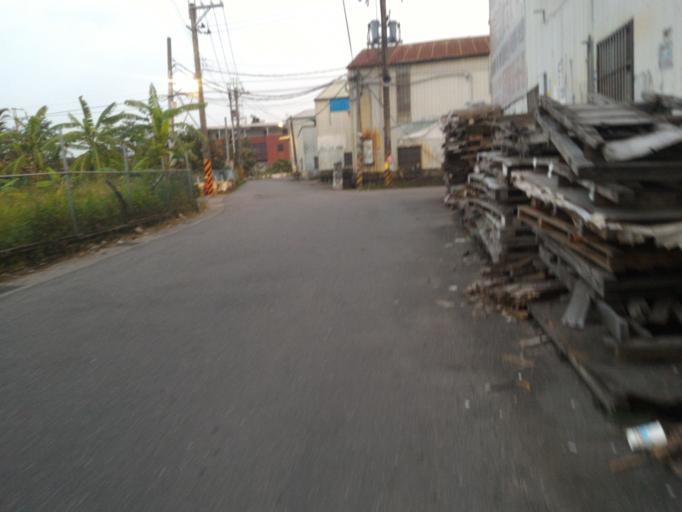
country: TW
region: Taiwan
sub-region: Taoyuan
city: Taoyuan
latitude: 24.9491
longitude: 121.4010
